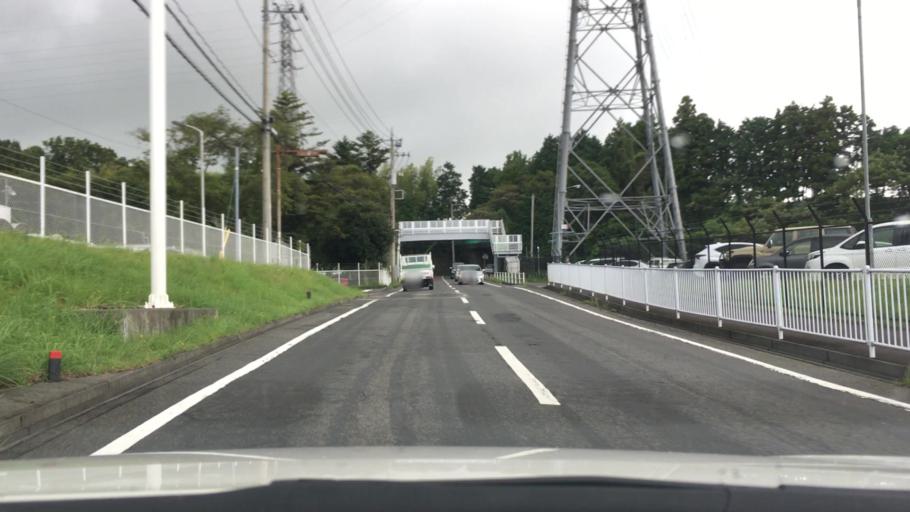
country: JP
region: Shizuoka
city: Gotemba
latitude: 35.2278
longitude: 138.8917
